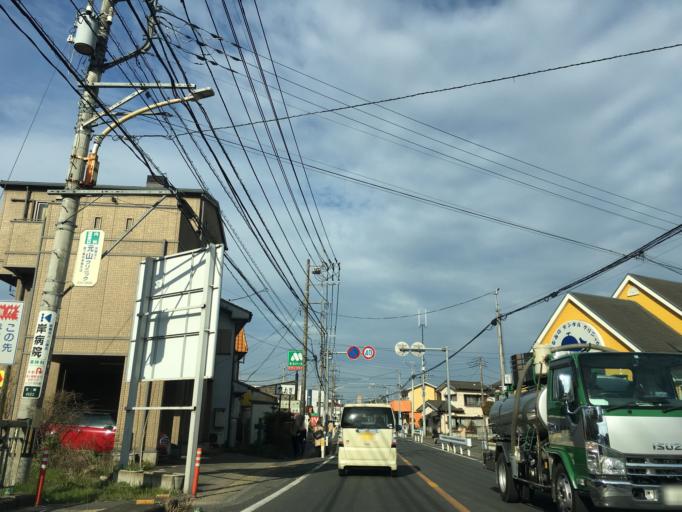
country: JP
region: Saitama
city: Sakado
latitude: 35.9083
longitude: 139.4122
